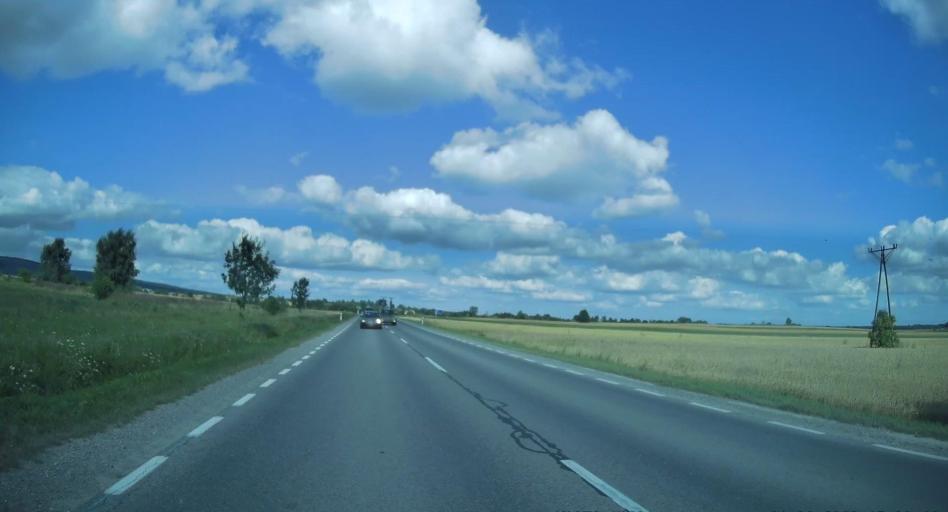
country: PL
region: Swietokrzyskie
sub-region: Powiat kielecki
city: Lagow
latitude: 50.7896
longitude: 21.1328
